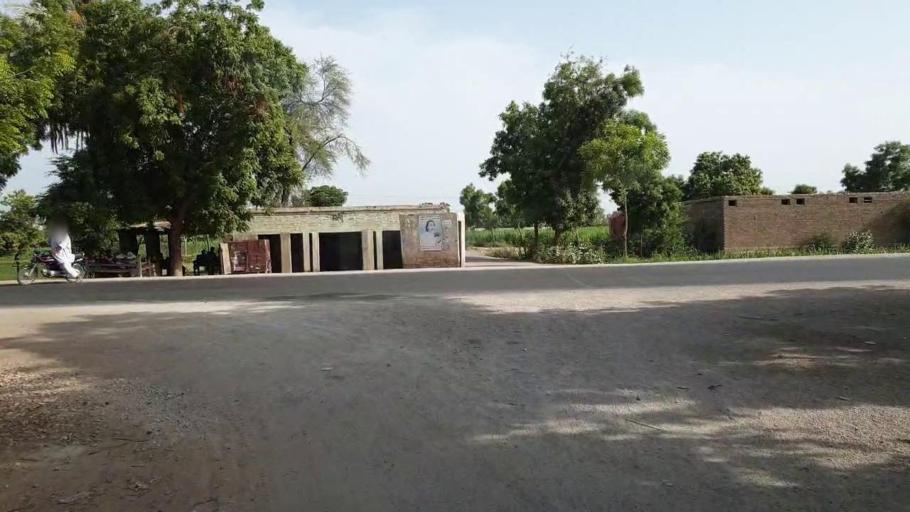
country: PK
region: Sindh
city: Sakrand
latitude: 26.2448
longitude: 68.2846
